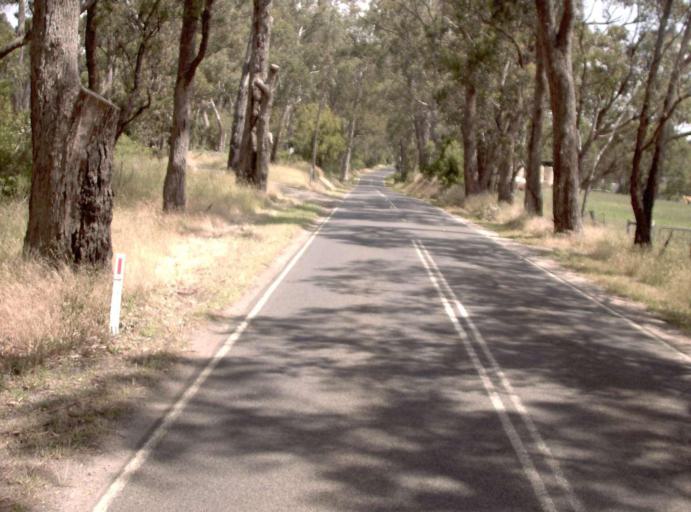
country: AU
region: Victoria
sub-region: Latrobe
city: Traralgon
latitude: -38.2902
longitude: 146.5397
